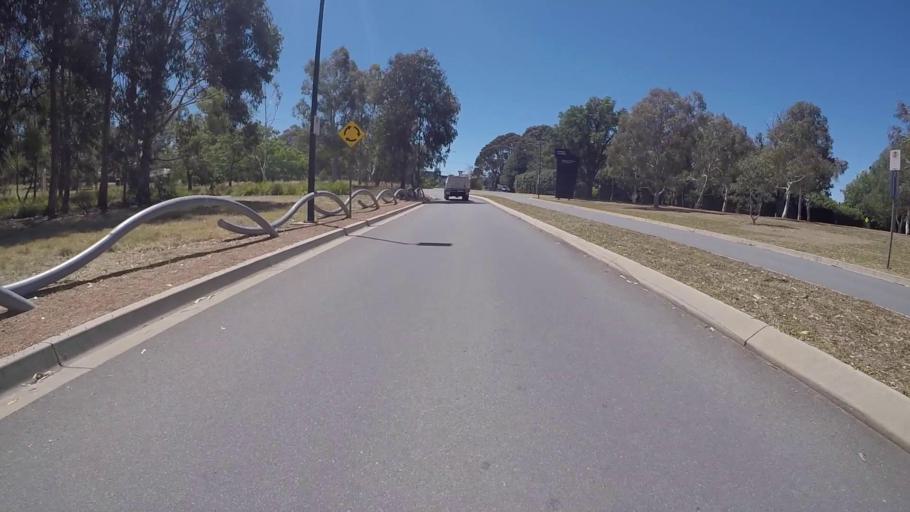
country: AU
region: Australian Capital Territory
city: Canberra
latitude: -35.2909
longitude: 149.1175
